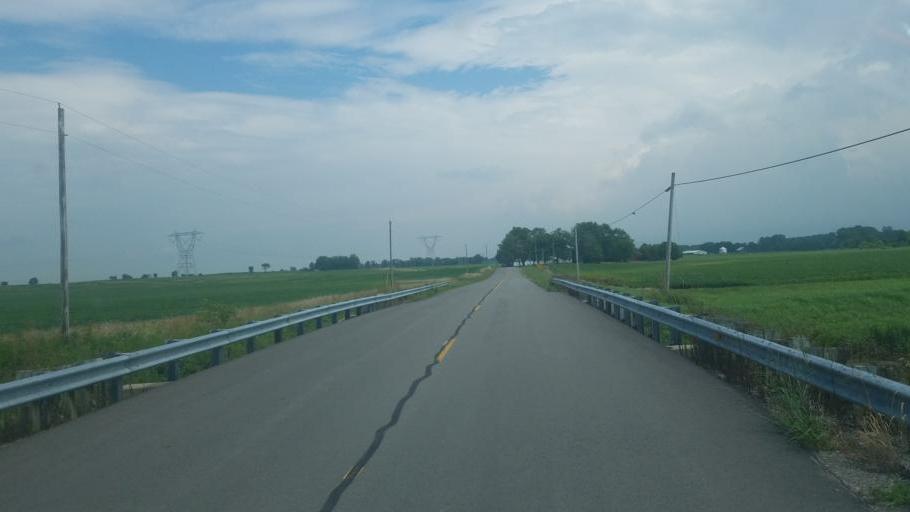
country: US
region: Ohio
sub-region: Logan County
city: Northwood
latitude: 40.3915
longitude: -83.5920
